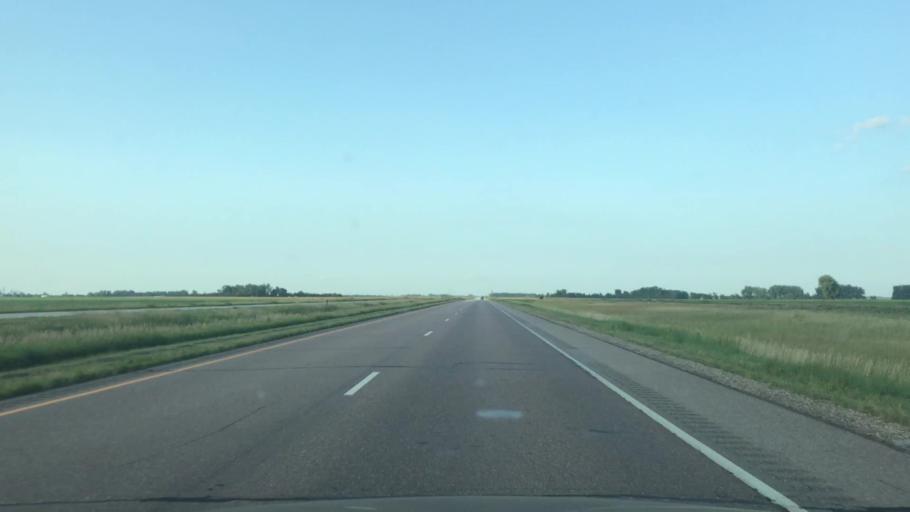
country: US
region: Minnesota
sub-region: Nobles County
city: Worthington
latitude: 43.7364
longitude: -95.4132
